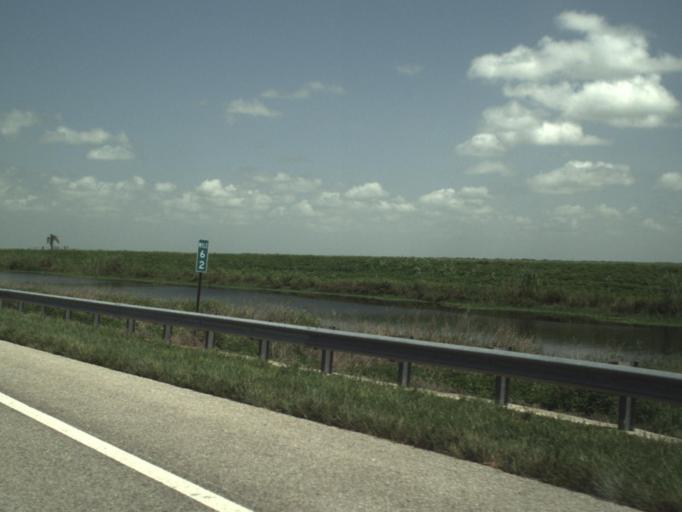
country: US
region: Florida
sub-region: Palm Beach County
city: Belle Glade Camp
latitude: 26.5087
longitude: -80.6723
